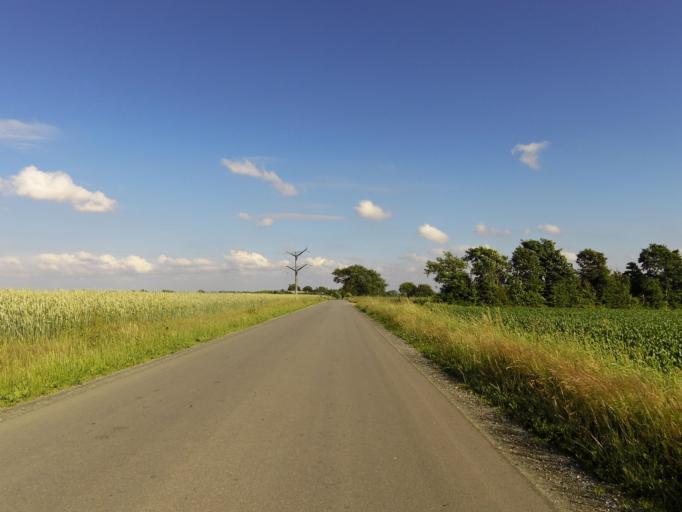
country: DK
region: South Denmark
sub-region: Vejen Kommune
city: Rodding
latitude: 55.3318
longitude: 9.1649
